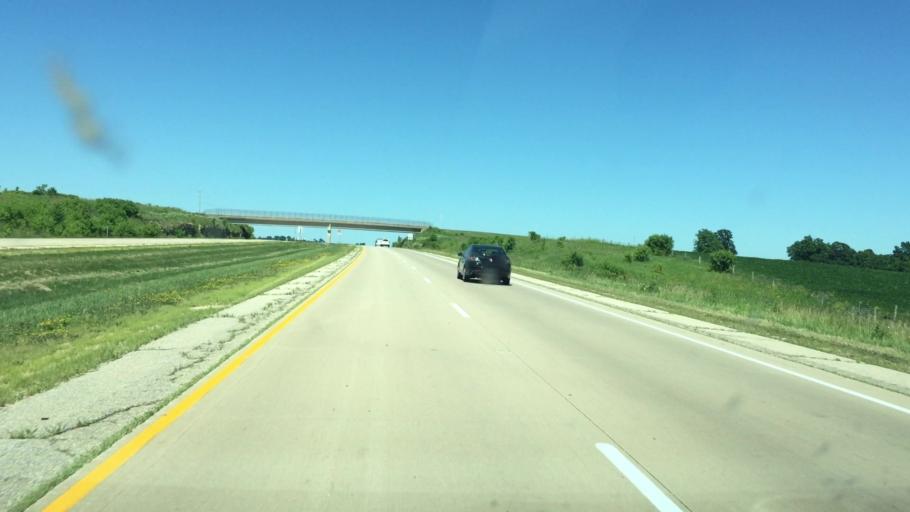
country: US
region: Wisconsin
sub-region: Iowa County
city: Mineral Point
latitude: 42.8923
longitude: -90.1578
